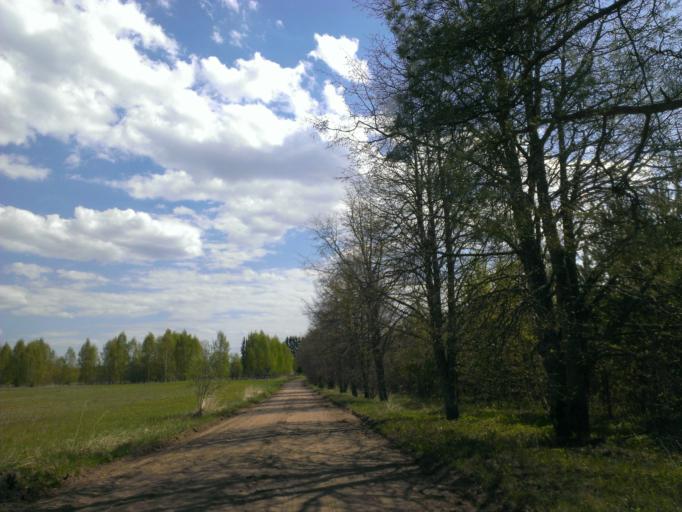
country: LV
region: Saulkrastu
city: Saulkrasti
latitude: 57.3618
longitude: 24.4898
